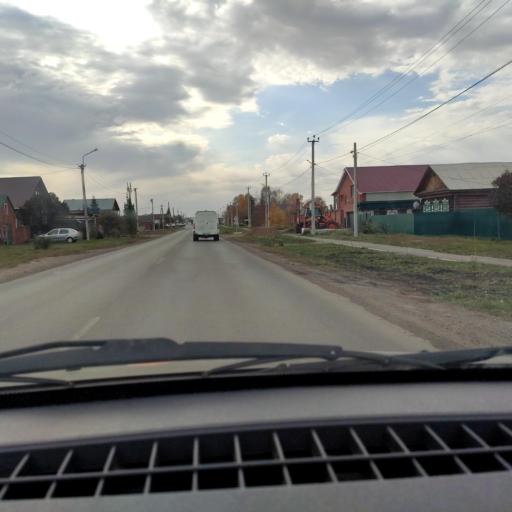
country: RU
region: Bashkortostan
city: Ufa
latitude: 54.6179
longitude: 55.9047
